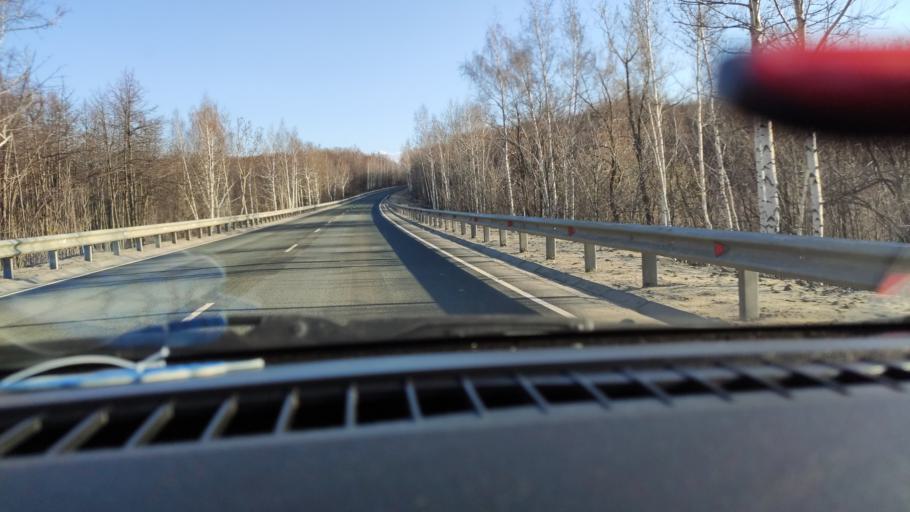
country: RU
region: Saratov
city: Khvalynsk
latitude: 52.4445
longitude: 48.0099
